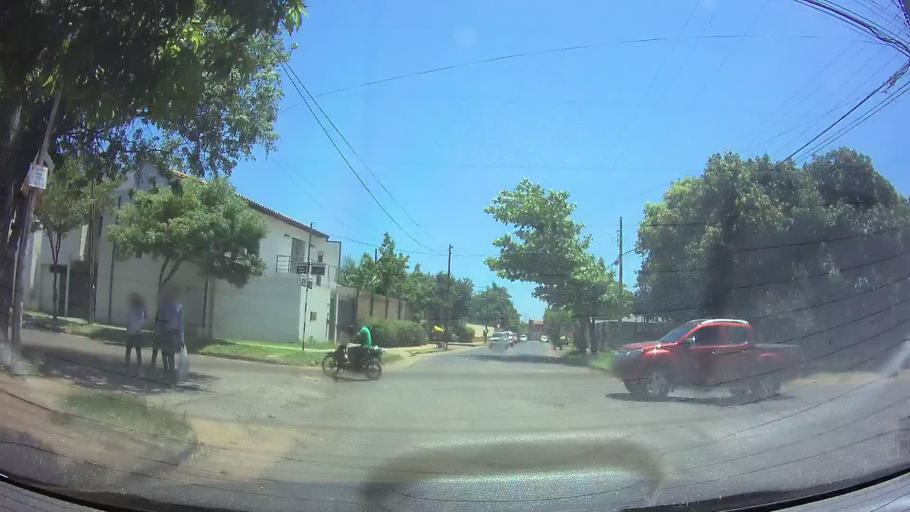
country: PY
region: Central
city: San Lorenzo
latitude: -25.2693
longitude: -57.5066
